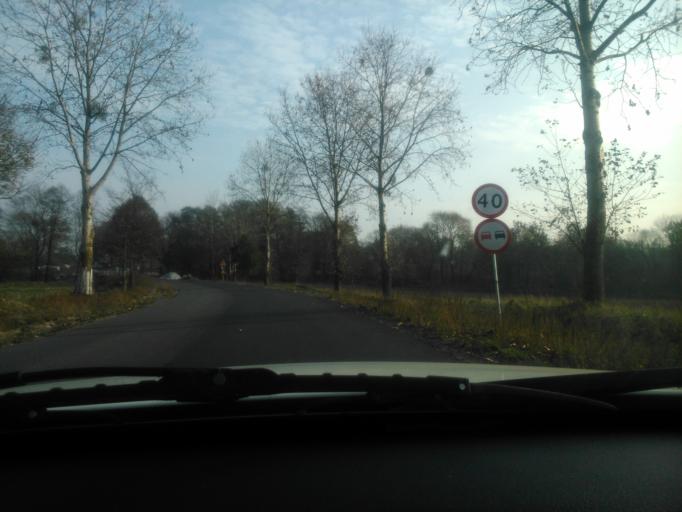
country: PL
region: Warmian-Masurian Voivodeship
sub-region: Powiat dzialdowski
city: Lidzbark
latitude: 53.2578
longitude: 19.8653
